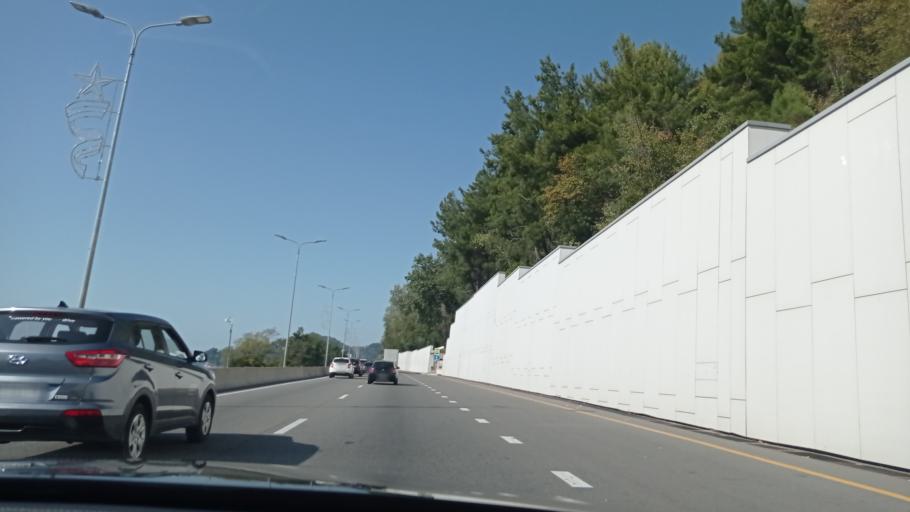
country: RU
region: Krasnodarskiy
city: Kudepsta
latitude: 43.5003
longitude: 39.8786
